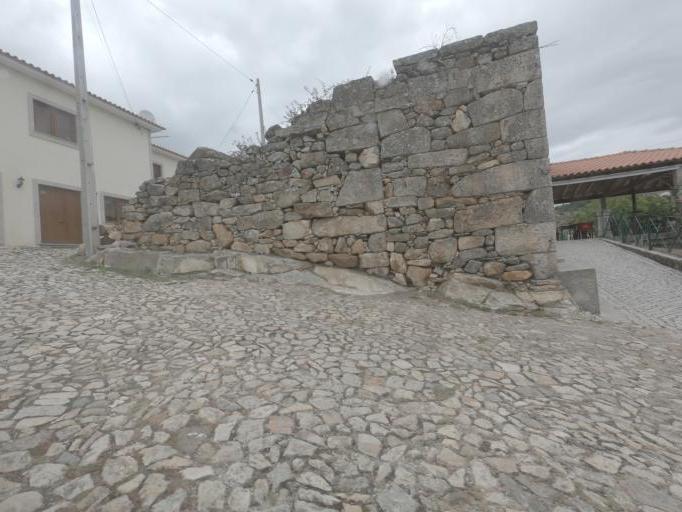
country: PT
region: Vila Real
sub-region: Sabrosa
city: Sabrosa
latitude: 41.2675
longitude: -7.5029
